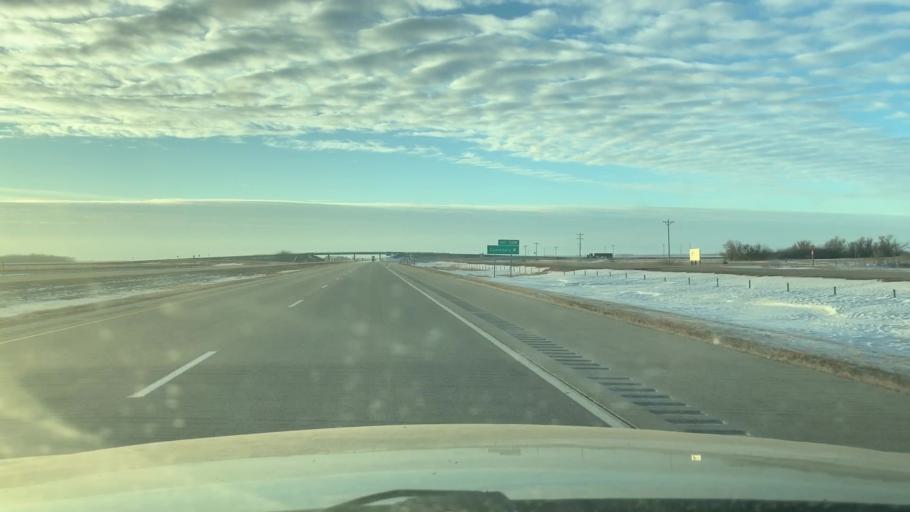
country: US
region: North Dakota
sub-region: Cass County
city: Casselton
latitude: 46.8761
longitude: -97.2552
